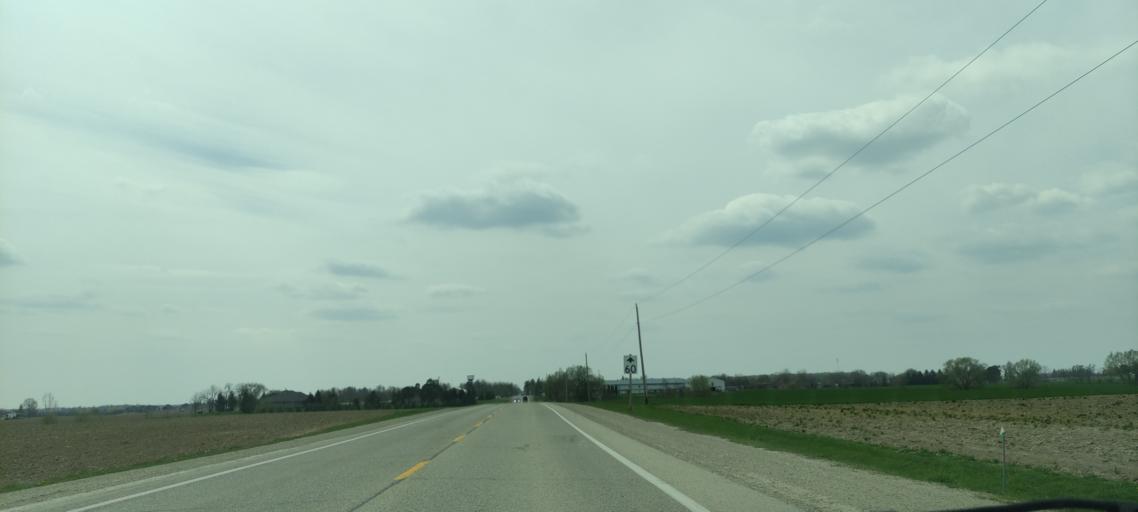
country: CA
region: Ontario
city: Stratford
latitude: 43.3278
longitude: -80.8147
